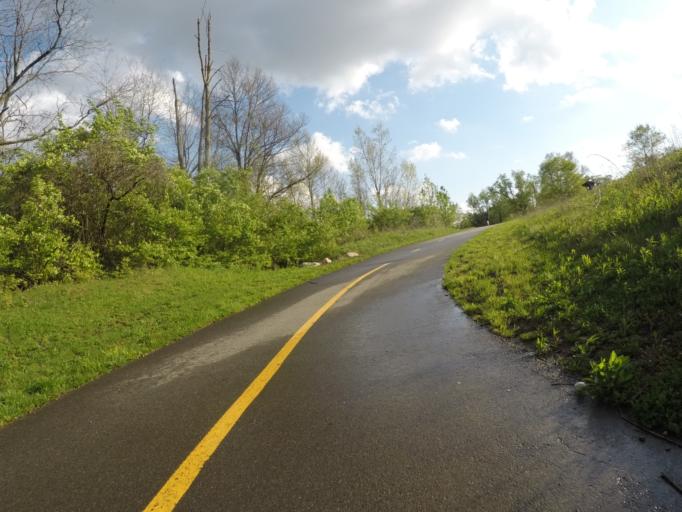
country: US
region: Ohio
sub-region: Franklin County
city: Bexley
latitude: 39.9904
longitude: -82.9381
